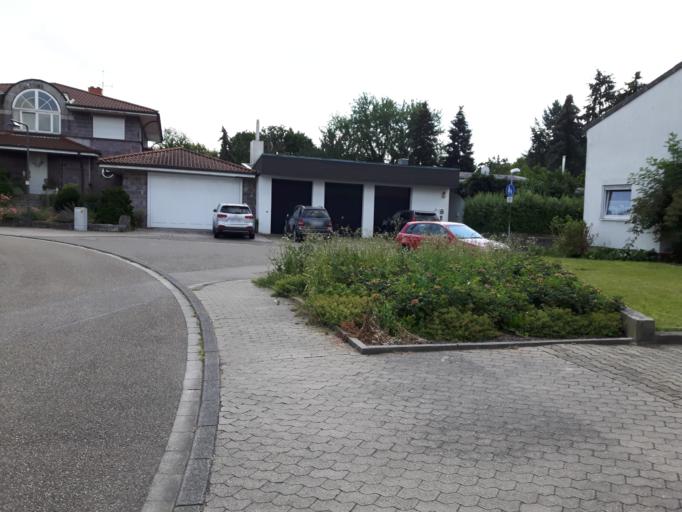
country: DE
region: Baden-Wuerttemberg
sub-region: Karlsruhe Region
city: Karlsdorf-Neuthard
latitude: 49.0976
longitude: 8.5316
